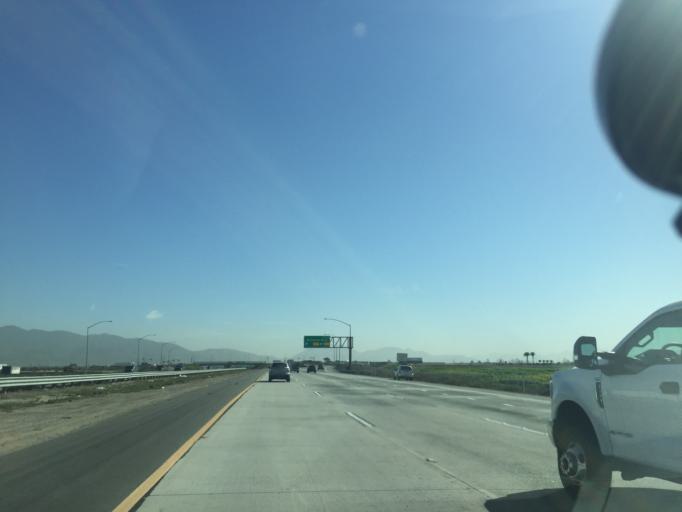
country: MX
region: Baja California
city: Tijuana
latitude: 32.5647
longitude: -116.9869
